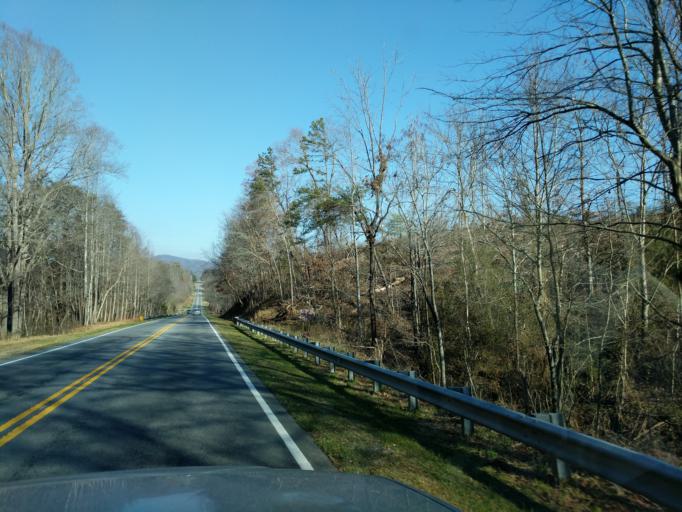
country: US
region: North Carolina
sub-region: McDowell County
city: West Marion
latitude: 35.6018
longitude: -81.9843
